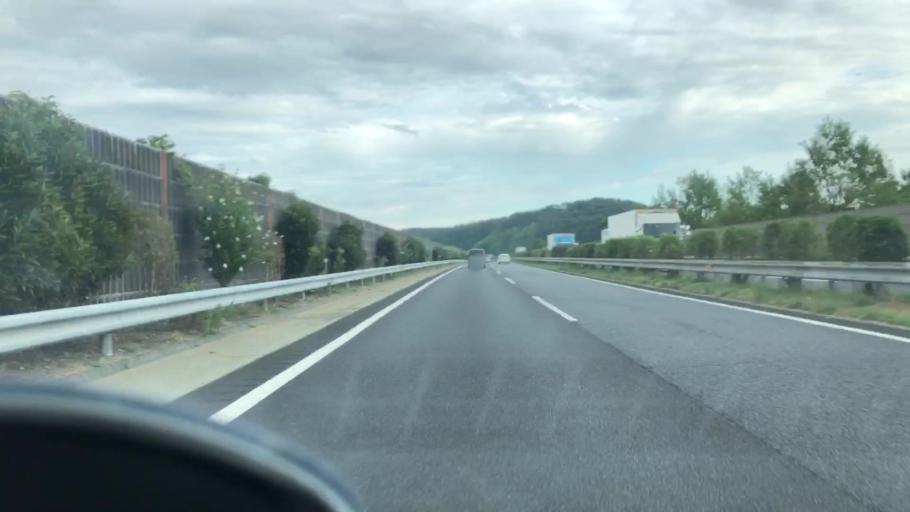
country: JP
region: Hyogo
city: Yashiro
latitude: 34.9048
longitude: 135.0656
